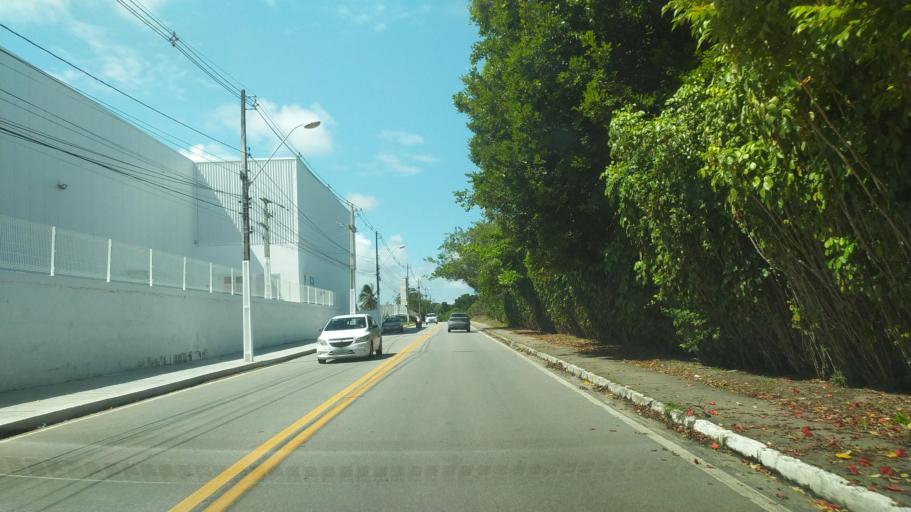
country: BR
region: Alagoas
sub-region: Maceio
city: Maceio
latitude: -9.6038
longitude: -35.7424
